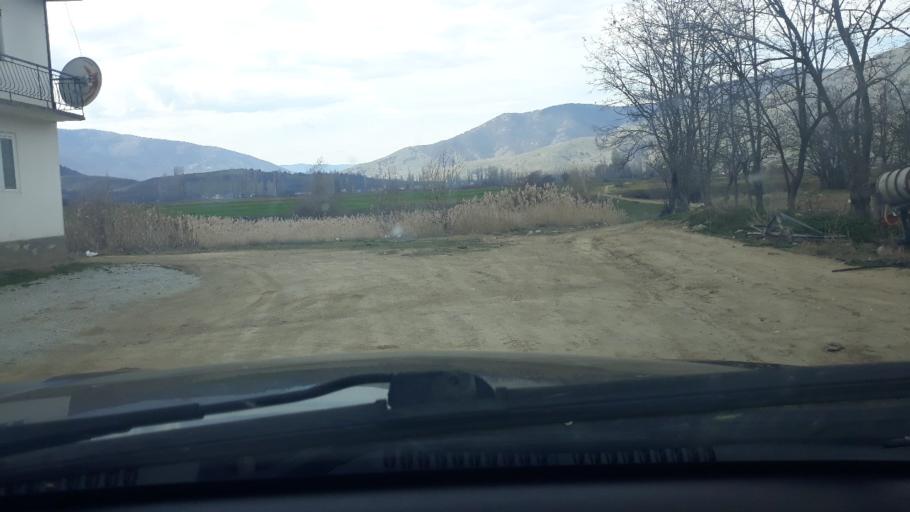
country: MK
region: Krusevo
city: Bucin
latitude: 41.2785
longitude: 21.3358
